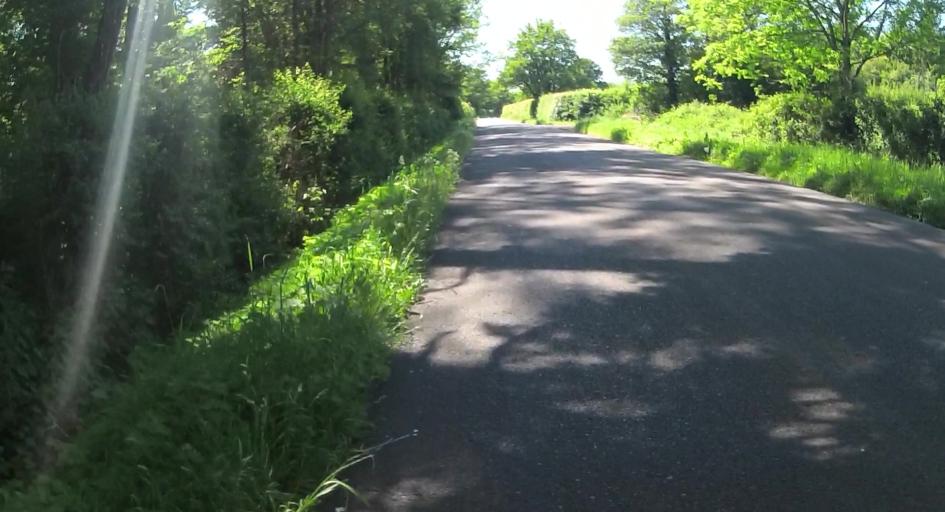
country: GB
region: England
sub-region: West Berkshire
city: Stratfield Mortimer
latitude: 51.3607
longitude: -0.9956
